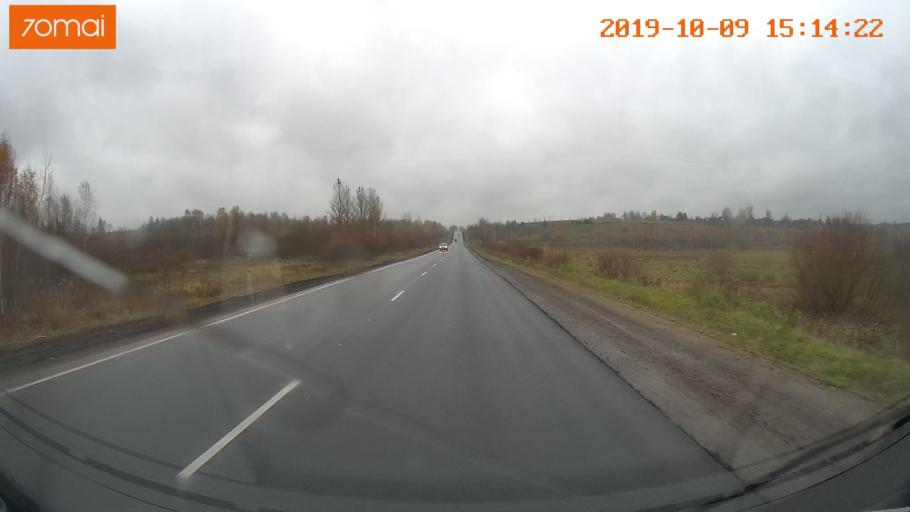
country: RU
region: Kostroma
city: Susanino
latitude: 58.1352
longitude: 41.6042
